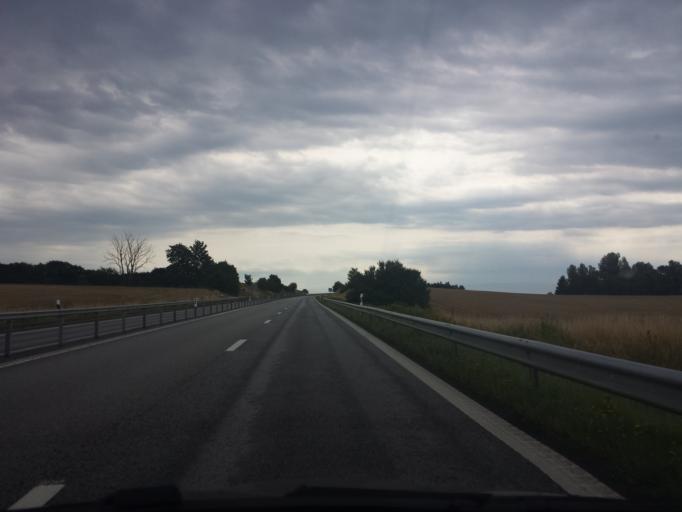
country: SE
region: Skane
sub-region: Ystads Kommun
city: Ystad
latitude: 55.4554
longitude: 13.7473
